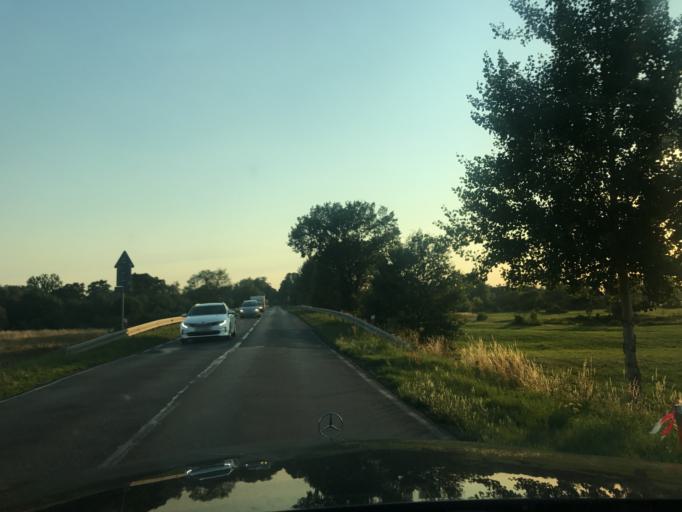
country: PL
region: Lublin Voivodeship
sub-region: Powiat lubartowski
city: Lubartow
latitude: 51.4986
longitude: 22.6486
